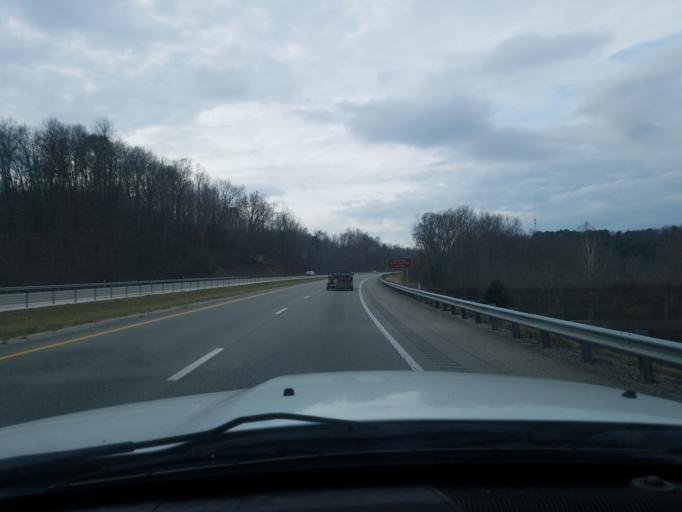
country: US
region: Kentucky
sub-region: Carter County
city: Olive Hill
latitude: 38.3227
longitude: -83.0876
